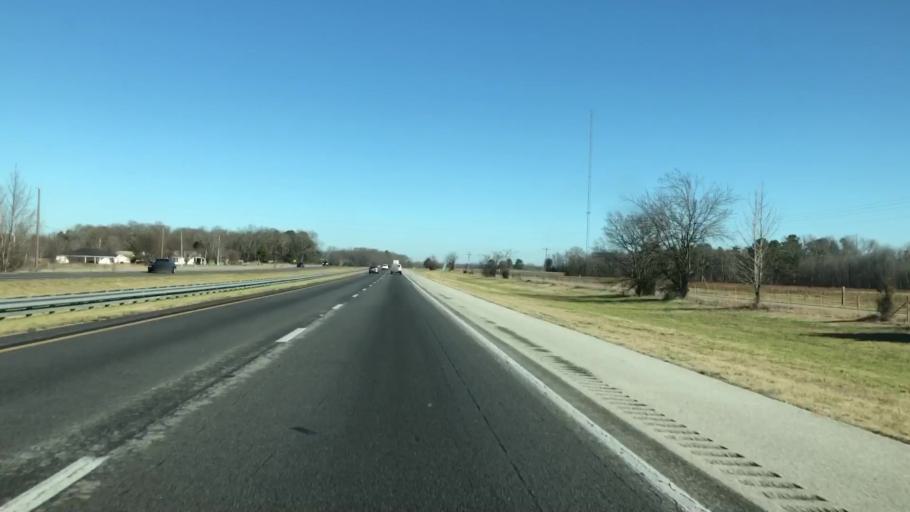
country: US
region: Alabama
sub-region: Limestone County
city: Athens
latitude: 34.8807
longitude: -86.9218
